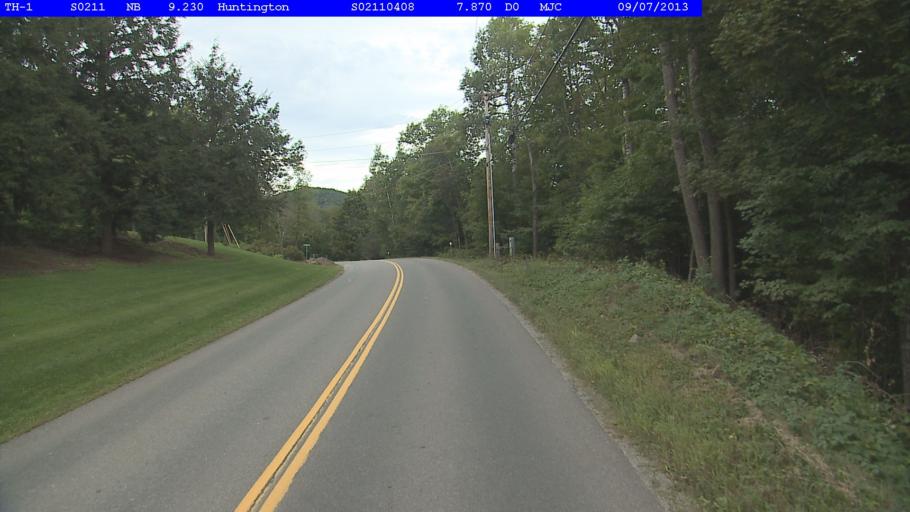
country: US
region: Vermont
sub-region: Chittenden County
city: Hinesburg
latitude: 44.3312
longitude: -72.9895
